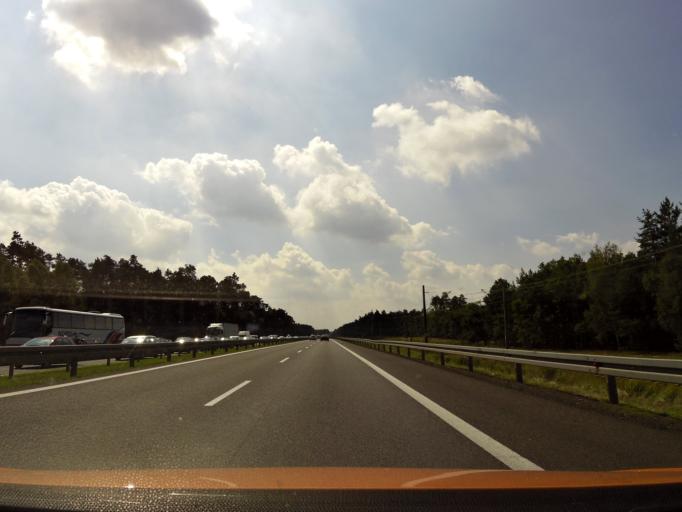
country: PL
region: West Pomeranian Voivodeship
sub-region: Powiat goleniowski
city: Goleniow
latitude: 53.4808
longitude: 14.7915
